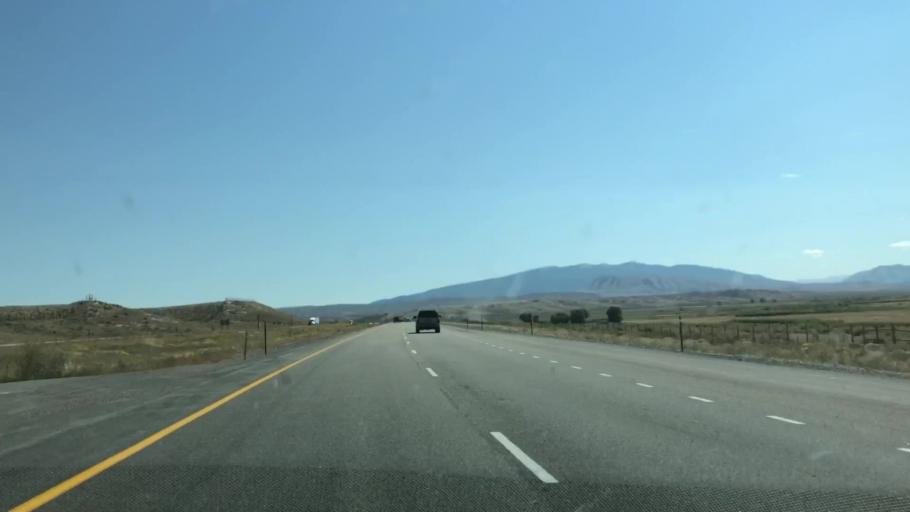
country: US
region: Wyoming
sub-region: Carbon County
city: Saratoga
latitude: 41.7410
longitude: -106.7667
